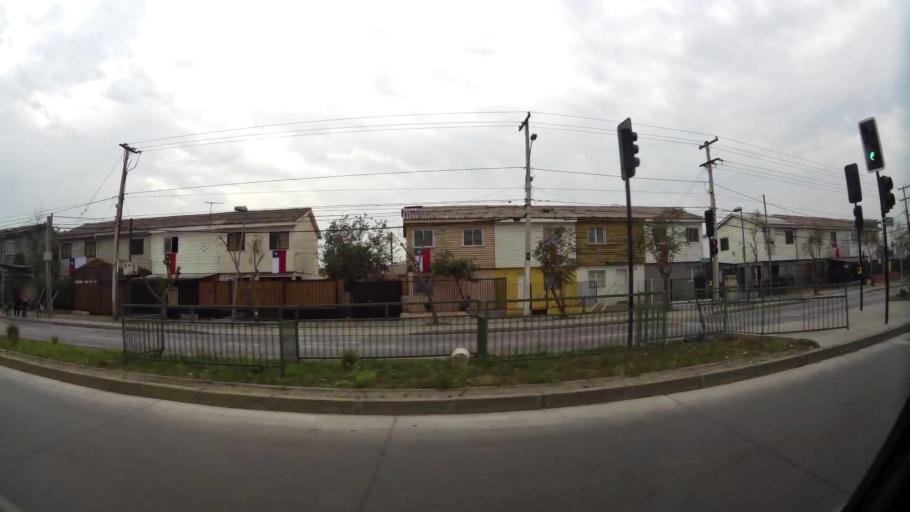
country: CL
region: Santiago Metropolitan
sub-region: Provincia de Santiago
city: Santiago
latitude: -33.4785
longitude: -70.6913
